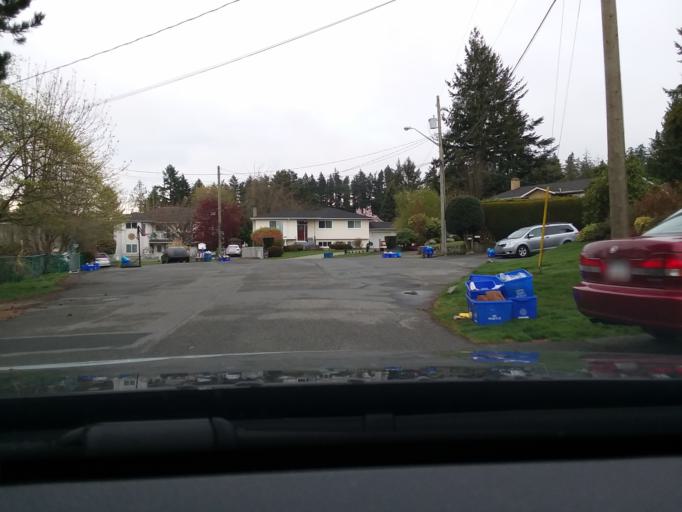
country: CA
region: British Columbia
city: North Saanich
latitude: 48.5525
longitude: -123.3954
